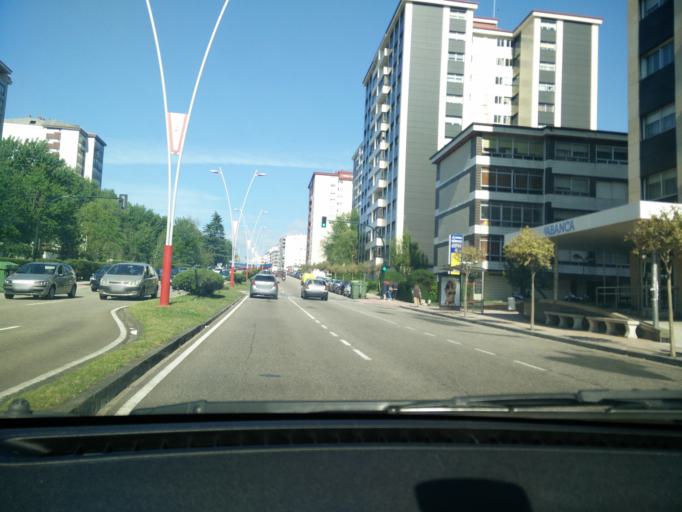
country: ES
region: Galicia
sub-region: Provincia de Pontevedra
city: Vigo
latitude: 42.2177
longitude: -8.7483
